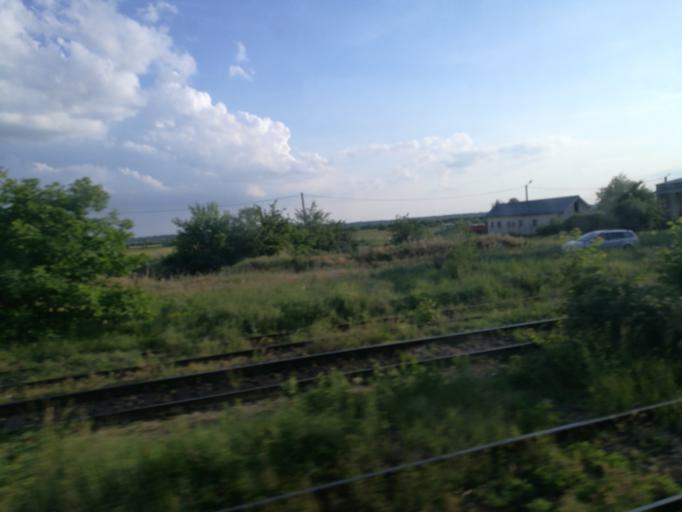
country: RO
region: Arges
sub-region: Comuna Calinesti
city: Calinesti
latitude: 44.8095
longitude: 25.0646
